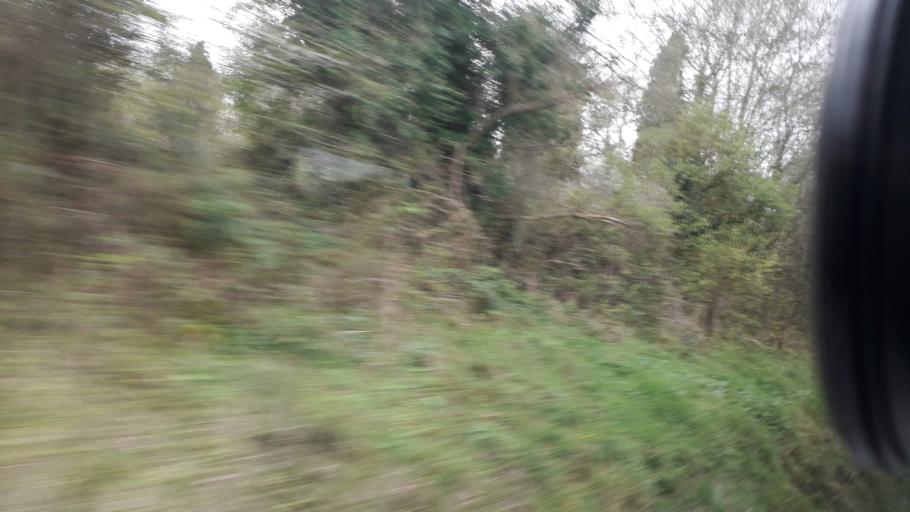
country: IE
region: Leinster
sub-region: An Longfort
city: Longford
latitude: 53.7245
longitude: -7.7702
